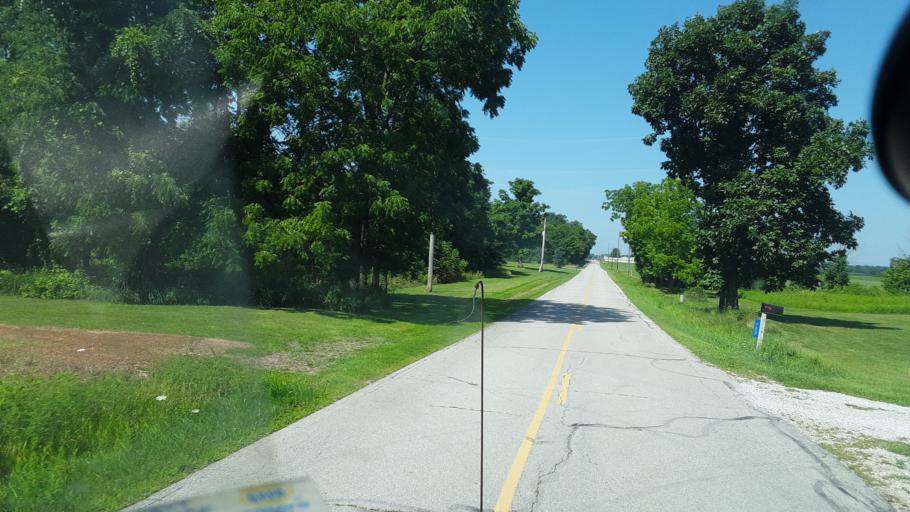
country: US
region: Ohio
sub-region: Crawford County
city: Bucyrus
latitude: 40.9066
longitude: -83.0779
